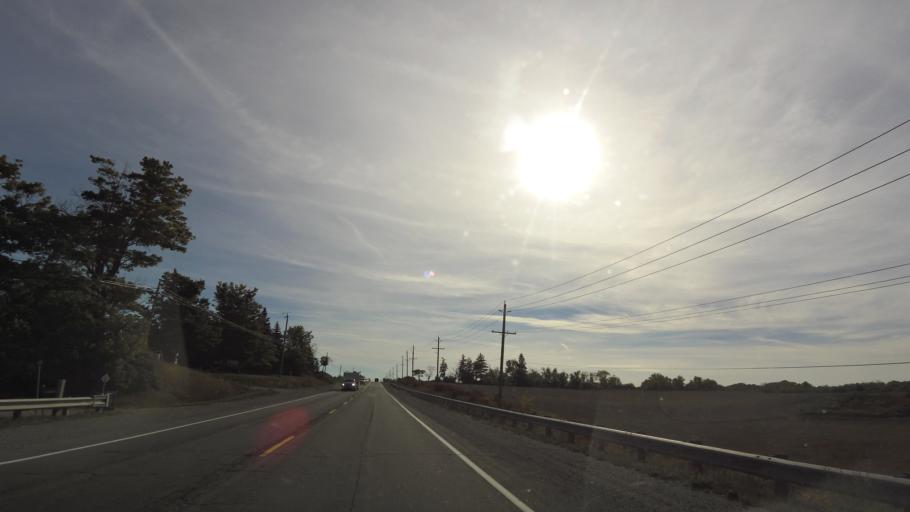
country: CA
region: Ontario
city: Ancaster
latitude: 43.0192
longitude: -80.0004
